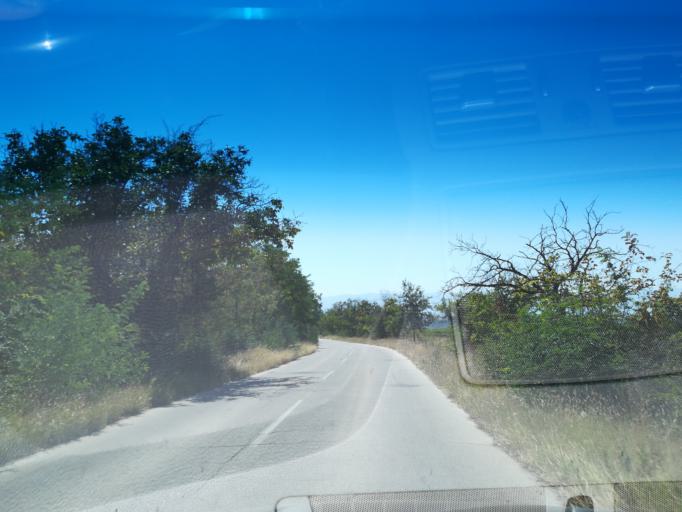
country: BG
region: Pazardzhik
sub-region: Obshtina Pazardzhik
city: Pazardzhik
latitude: 42.3113
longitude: 24.3999
